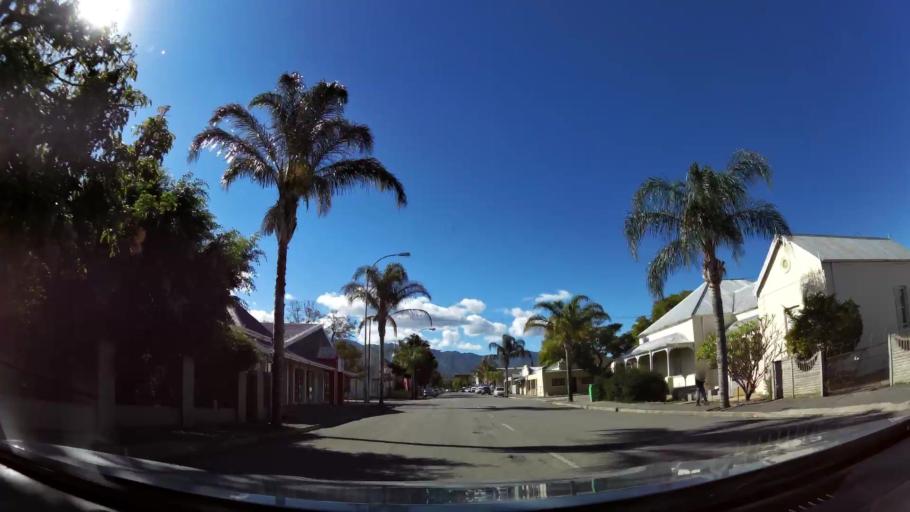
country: ZA
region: Western Cape
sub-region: Cape Winelands District Municipality
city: Ashton
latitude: -33.8052
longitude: 19.8794
